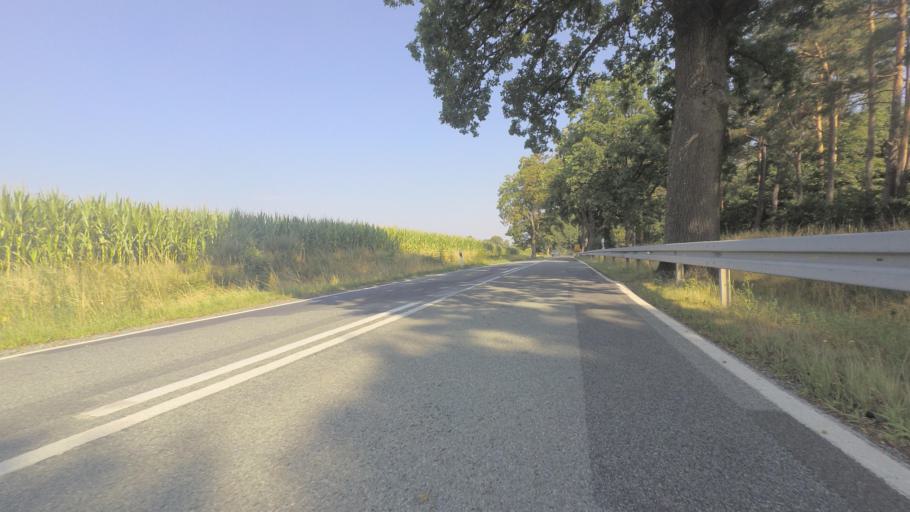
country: DE
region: Mecklenburg-Vorpommern
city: Grabowhofe
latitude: 53.6050
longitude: 12.4686
